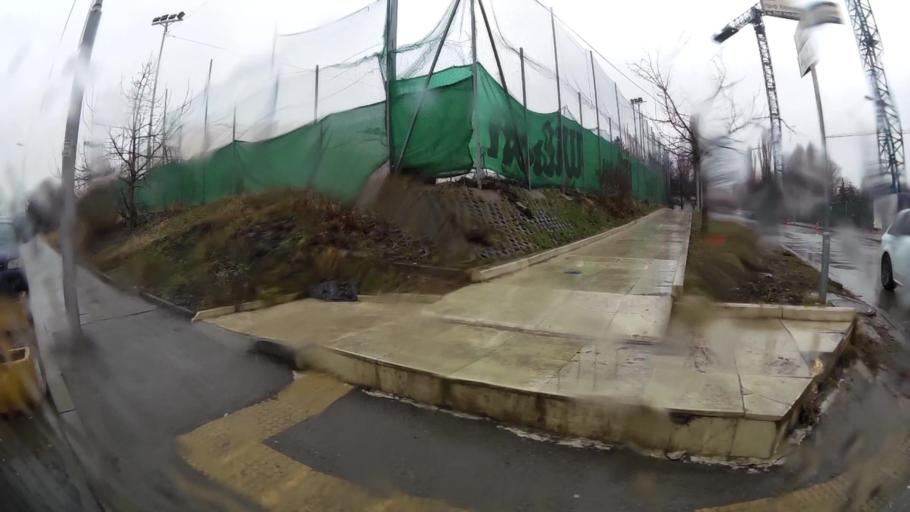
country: BG
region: Sofia-Capital
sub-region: Stolichna Obshtina
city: Sofia
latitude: 42.6612
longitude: 23.3547
